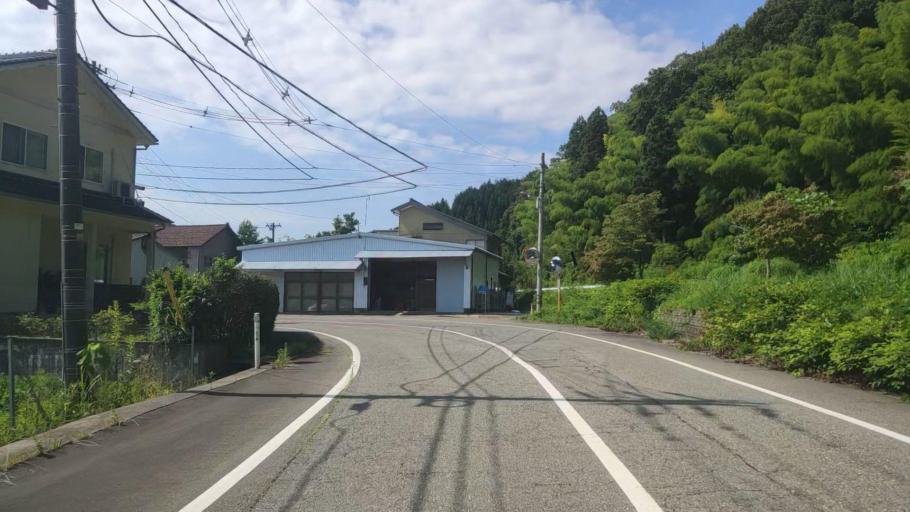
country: JP
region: Ishikawa
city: Komatsu
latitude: 36.3737
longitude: 136.4970
